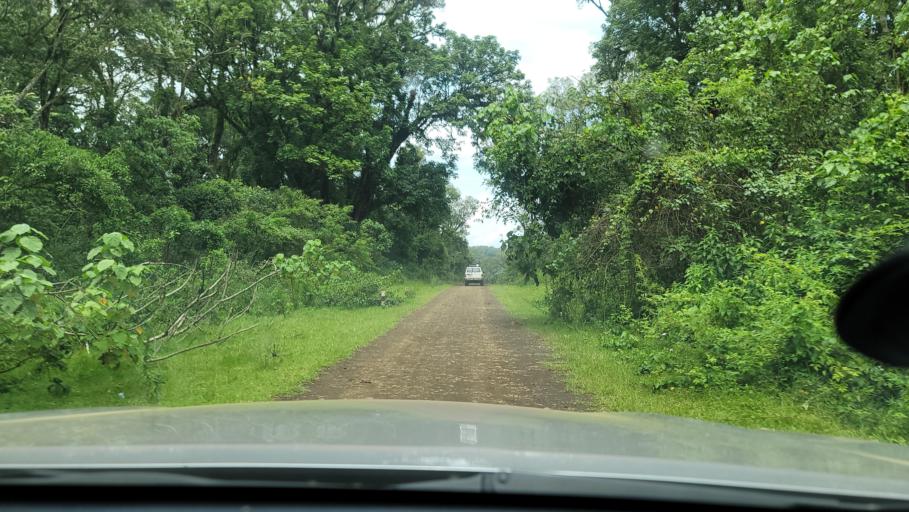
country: ET
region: Southern Nations, Nationalities, and People's Region
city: Bonga
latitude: 7.6520
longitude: 36.2466
